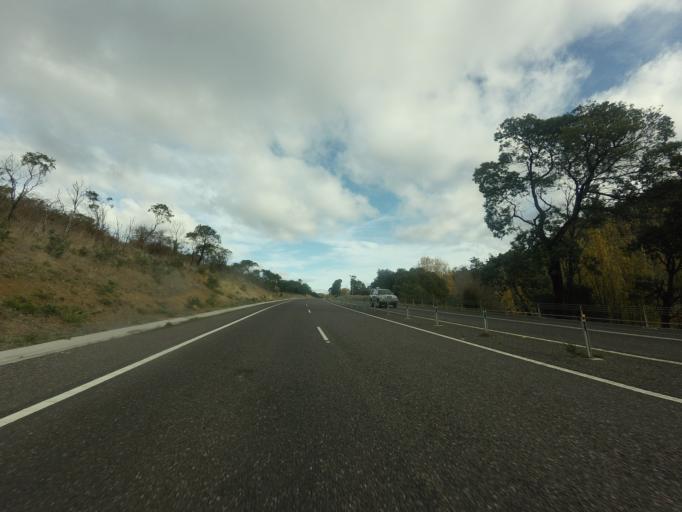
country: AU
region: Tasmania
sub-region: Brighton
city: Bridgewater
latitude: -42.5542
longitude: 147.2102
